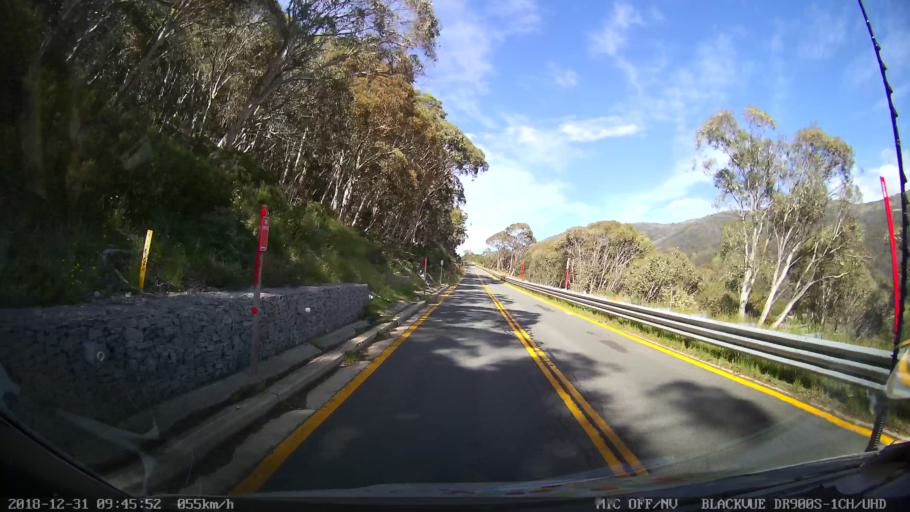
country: AU
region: New South Wales
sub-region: Snowy River
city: Jindabyne
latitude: -36.5015
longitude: 148.3143
